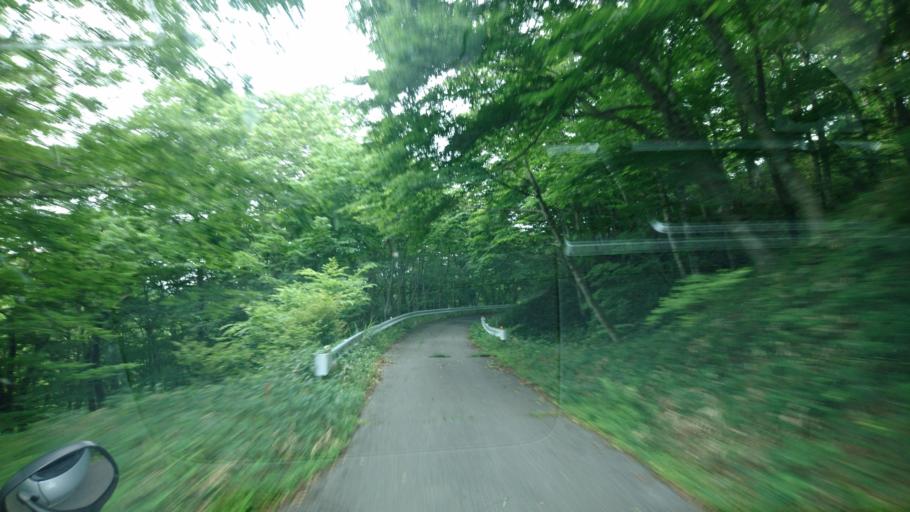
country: JP
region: Iwate
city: Ofunato
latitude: 39.1782
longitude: 141.7834
